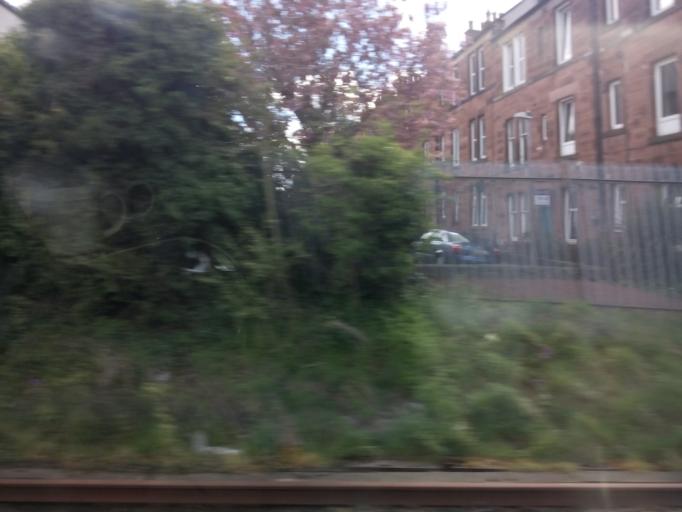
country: GB
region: Scotland
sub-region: West Lothian
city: Seafield
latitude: 55.9566
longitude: -3.1443
